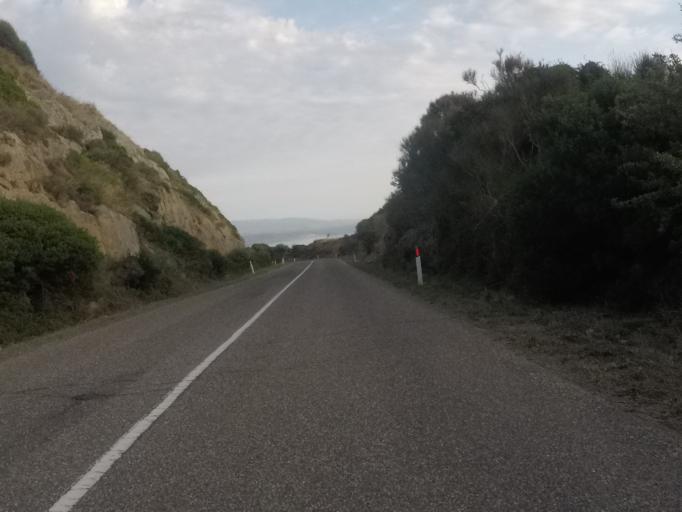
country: IT
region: Sardinia
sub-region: Provincia di Oristano
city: Montresta
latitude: 40.3658
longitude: 8.4101
